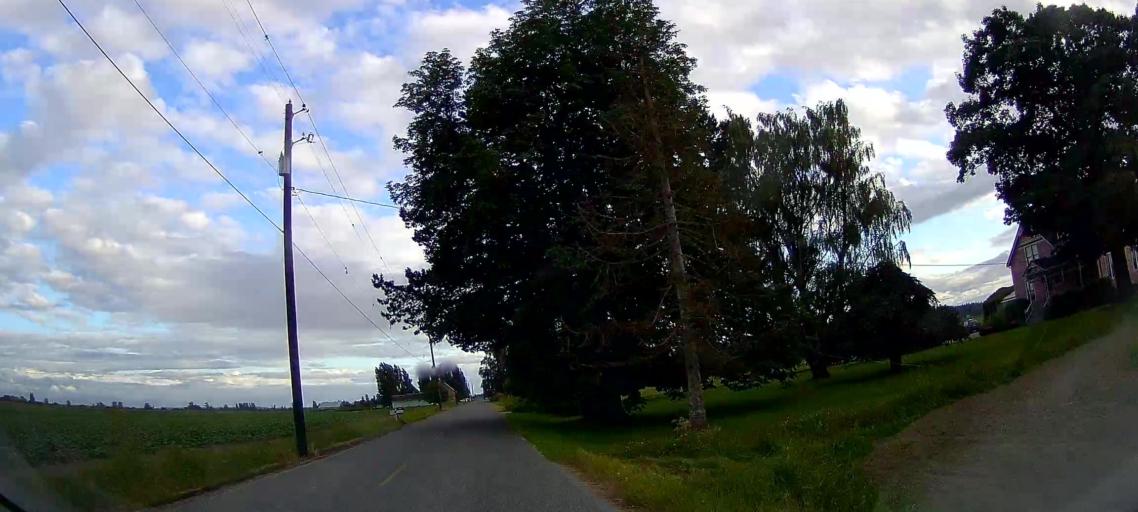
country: US
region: Washington
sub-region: Skagit County
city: Mount Vernon
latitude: 48.3804
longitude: -122.4000
